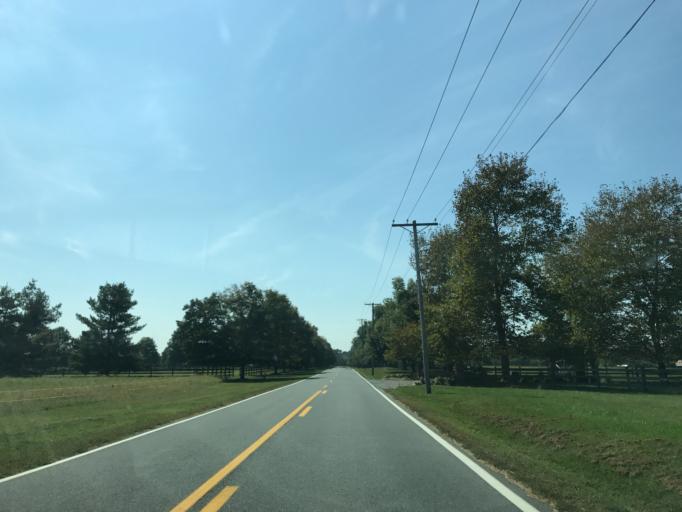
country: US
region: Delaware
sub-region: New Castle County
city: Middletown
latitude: 39.5053
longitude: -75.8005
